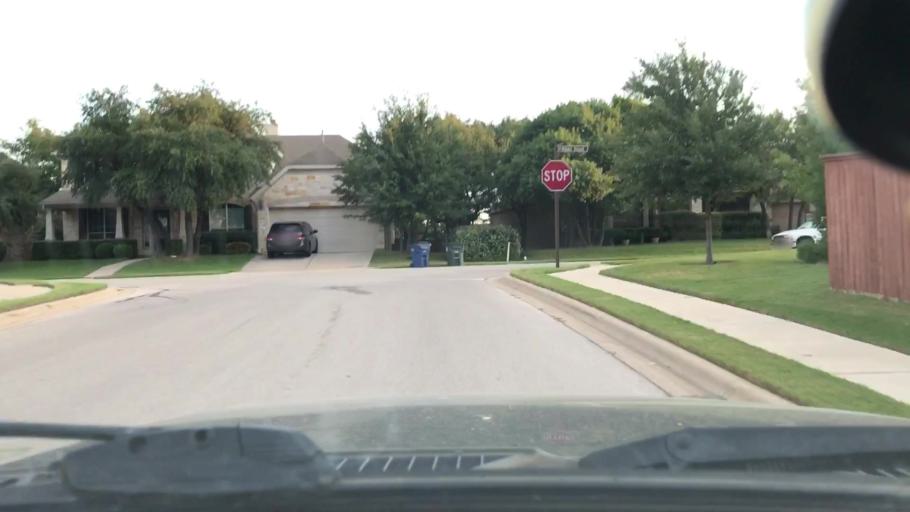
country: US
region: Texas
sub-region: Williamson County
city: Leander
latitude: 30.5405
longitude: -97.8656
